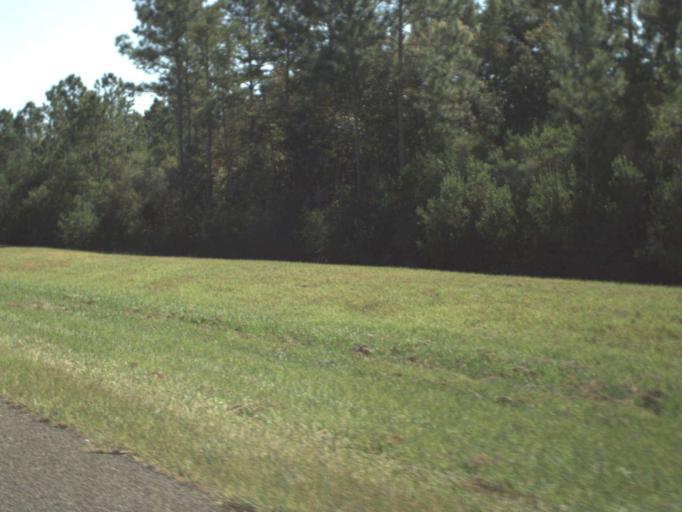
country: US
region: Florida
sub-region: Walton County
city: Seaside
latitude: 30.3568
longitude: -86.1205
